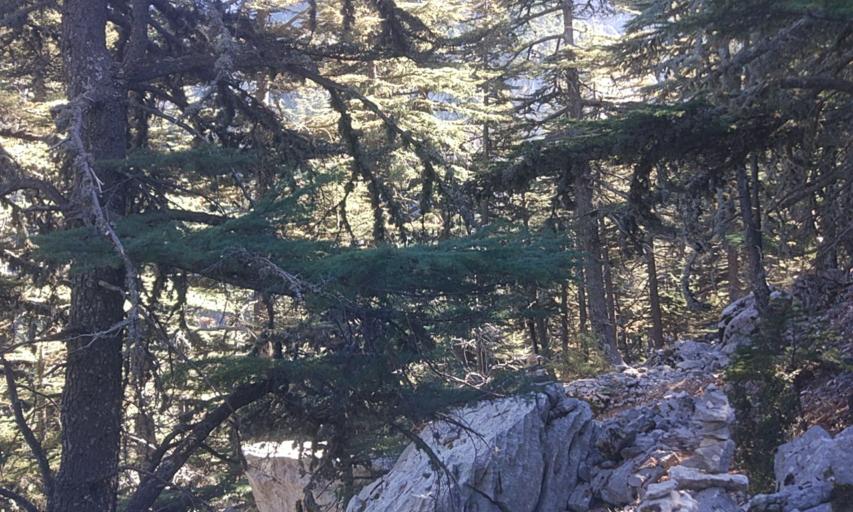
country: TR
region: Antalya
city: Altinyaka
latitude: 36.5565
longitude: 30.4154
